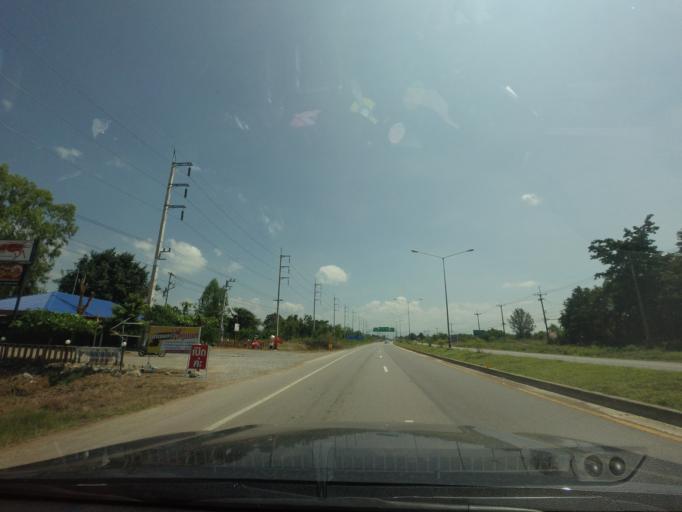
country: TH
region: Phetchabun
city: Lom Sak
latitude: 16.7671
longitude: 101.1825
